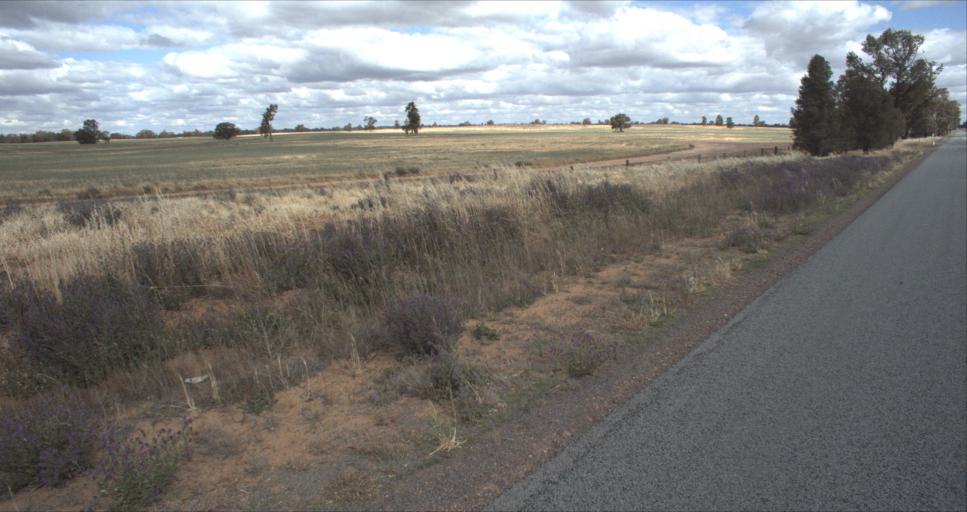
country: AU
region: New South Wales
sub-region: Leeton
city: Leeton
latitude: -34.6743
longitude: 146.3468
